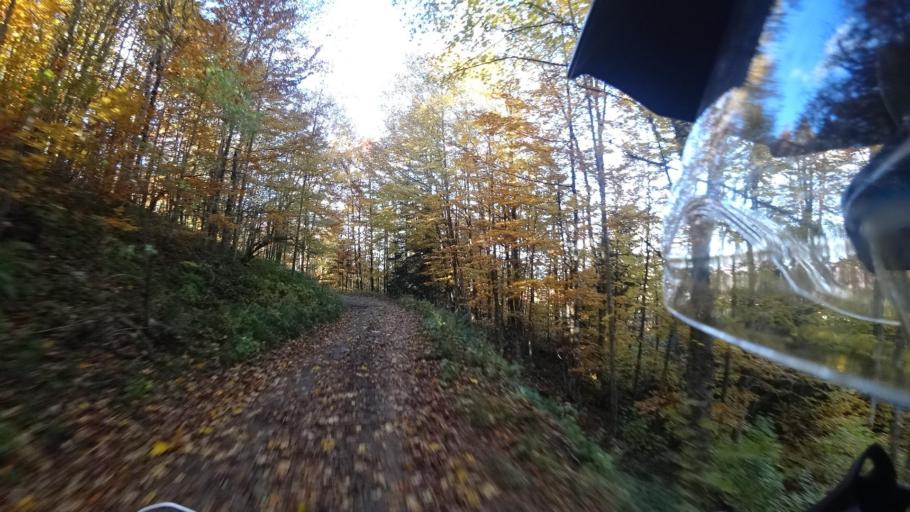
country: HR
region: Karlovacka
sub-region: Grad Ogulin
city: Ogulin
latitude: 45.1845
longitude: 15.1142
